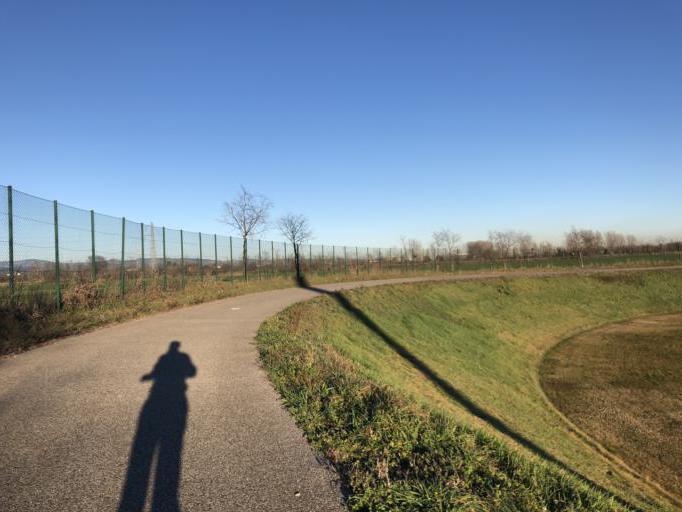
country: IT
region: Veneto
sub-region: Provincia di Verona
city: Caselle
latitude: 45.4203
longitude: 10.9007
